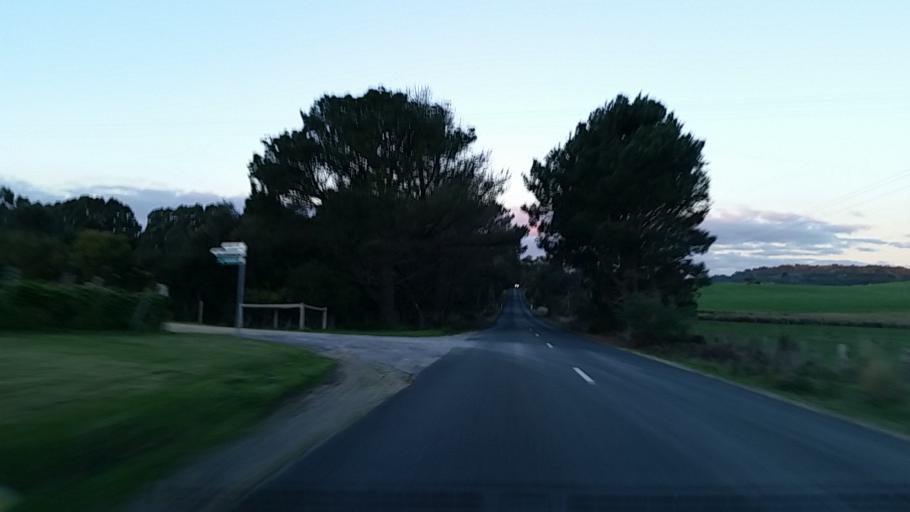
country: AU
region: South Australia
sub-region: Alexandrina
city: Mount Compass
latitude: -35.3189
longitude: 138.6219
